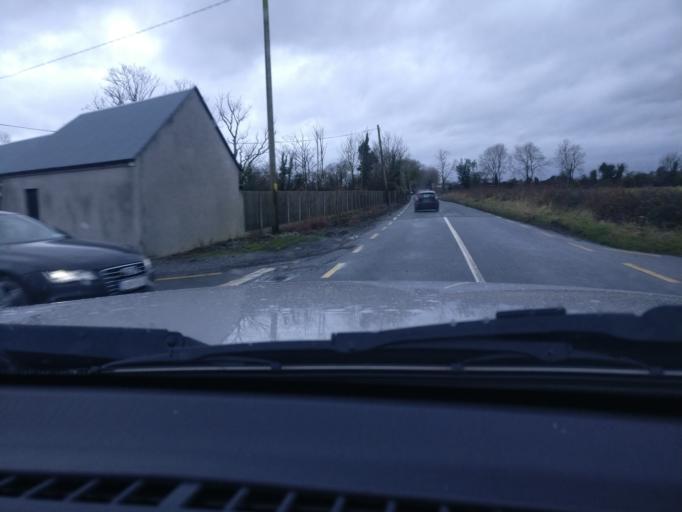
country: IE
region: Leinster
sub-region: An Mhi
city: Longwood
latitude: 53.4480
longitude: -6.9683
